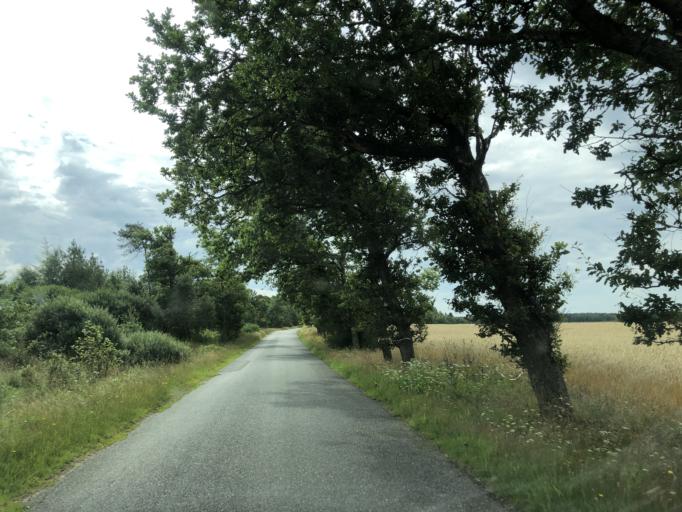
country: DK
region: Central Jutland
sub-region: Holstebro Kommune
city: Ulfborg
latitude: 56.2906
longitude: 8.4661
